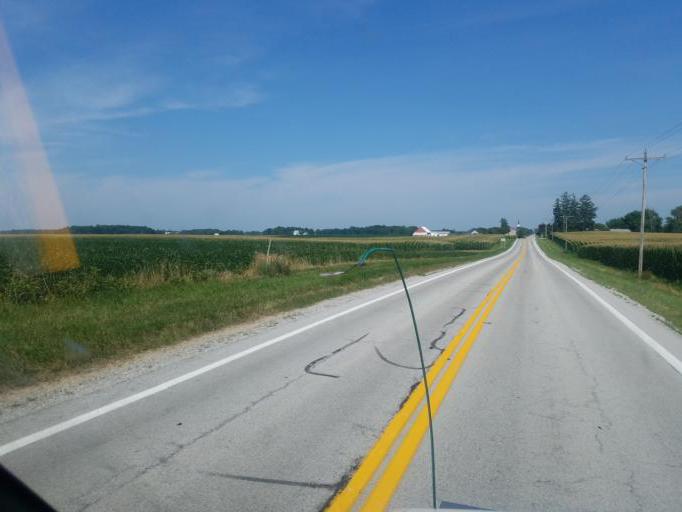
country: US
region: Ohio
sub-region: Shelby County
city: Botkins
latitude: 40.4966
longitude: -84.2434
